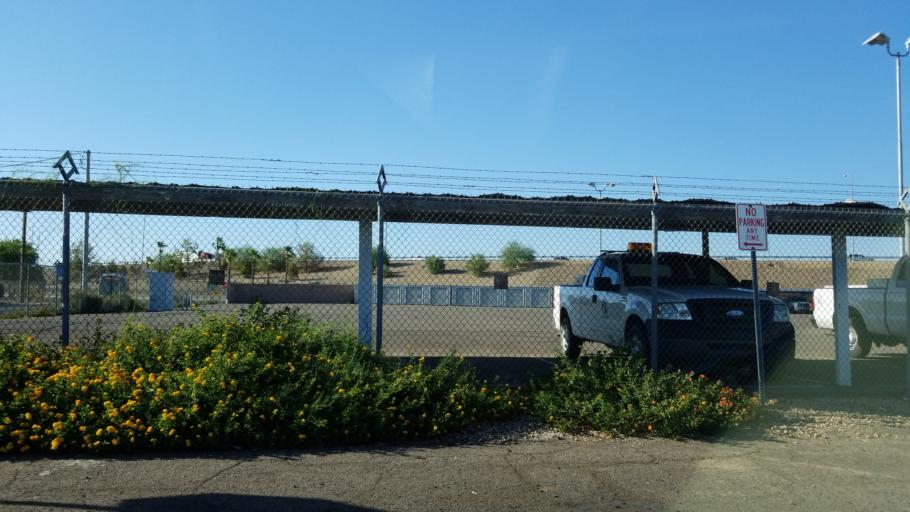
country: US
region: Arizona
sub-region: Maricopa County
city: Phoenix
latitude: 33.4282
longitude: -112.1061
